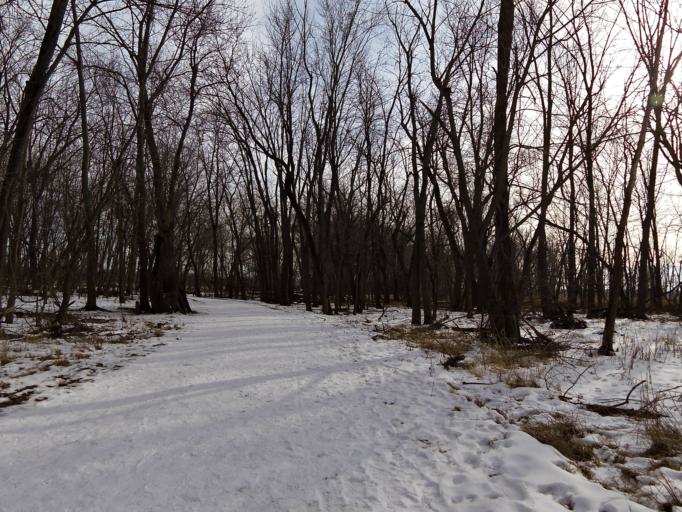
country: US
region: Minnesota
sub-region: Dakota County
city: Eagan
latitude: 44.8566
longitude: -93.2143
